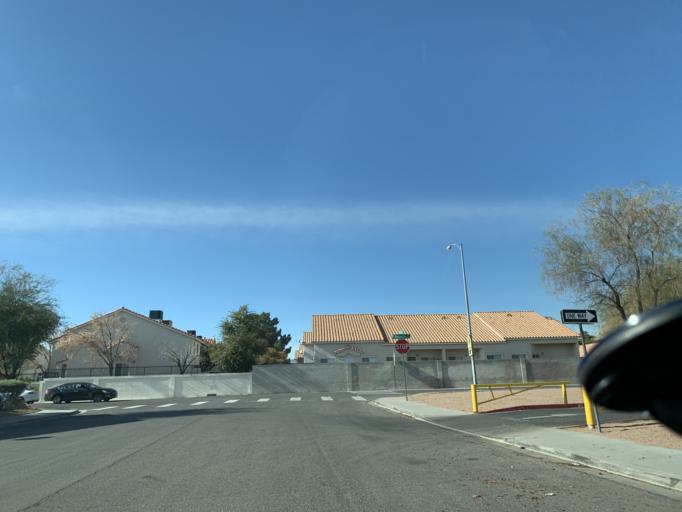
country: US
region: Nevada
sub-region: Clark County
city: Spring Valley
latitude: 36.0948
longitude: -115.2204
